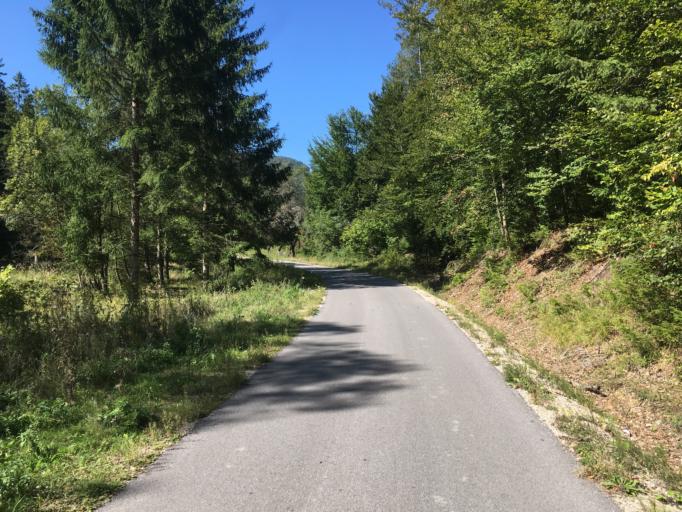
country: SK
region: Trenciansky
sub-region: Okres Povazska Bystrica
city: Povazska Bystrica
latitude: 49.0092
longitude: 18.4526
